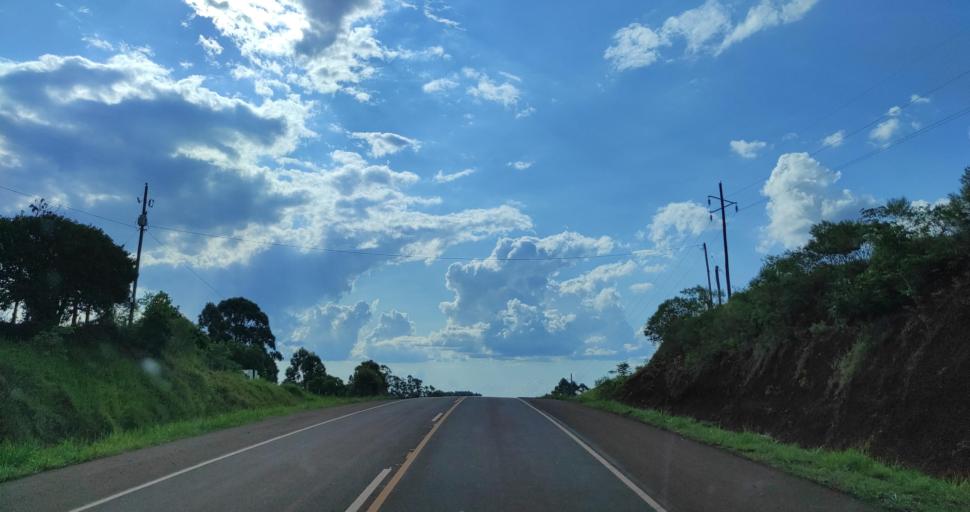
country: AR
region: Misiones
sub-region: Departamento de San Pedro
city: San Pedro
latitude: -26.3747
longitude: -53.9287
